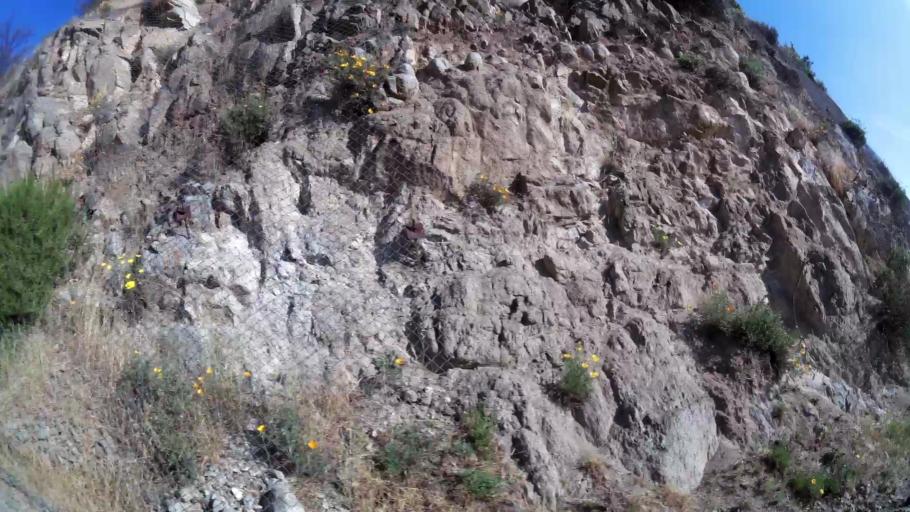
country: CL
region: Santiago Metropolitan
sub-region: Provincia de Santiago
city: Villa Presidente Frei, Nunoa, Santiago, Chile
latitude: -33.3637
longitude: -70.4736
